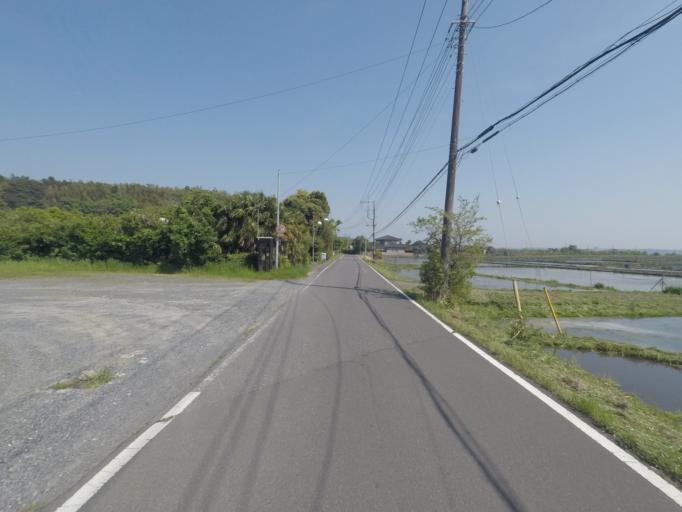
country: JP
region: Ibaraki
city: Ami
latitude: 36.0721
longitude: 140.2751
